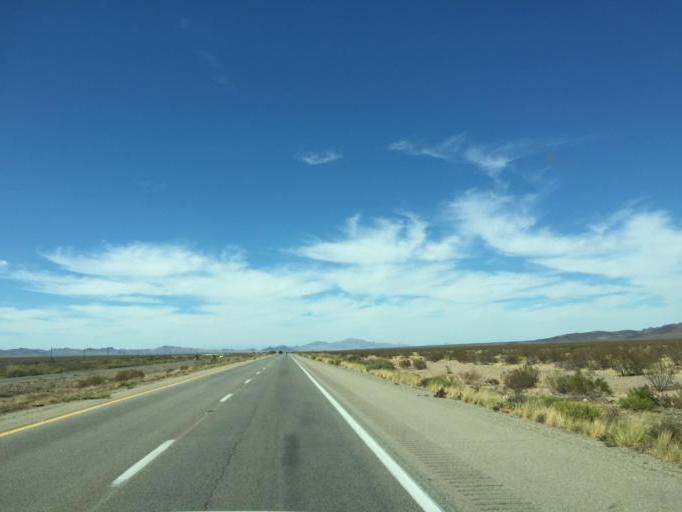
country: US
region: Arizona
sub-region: Mohave County
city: Dolan Springs
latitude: 35.5975
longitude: -114.3992
